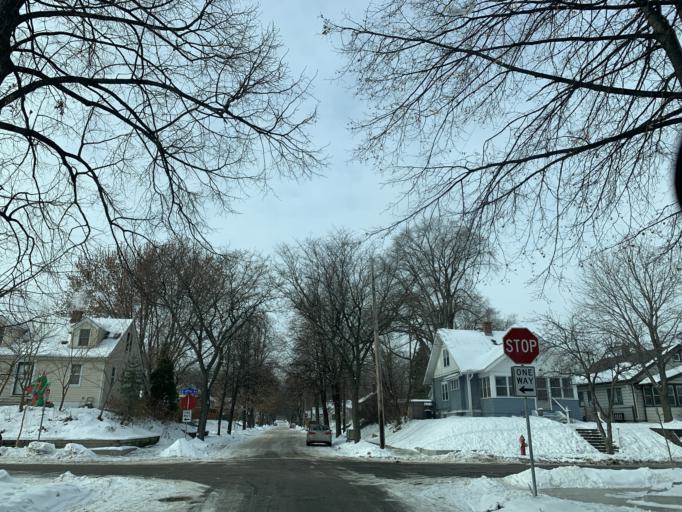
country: US
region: Minnesota
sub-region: Dakota County
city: Mendota Heights
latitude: 44.9072
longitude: -93.2060
